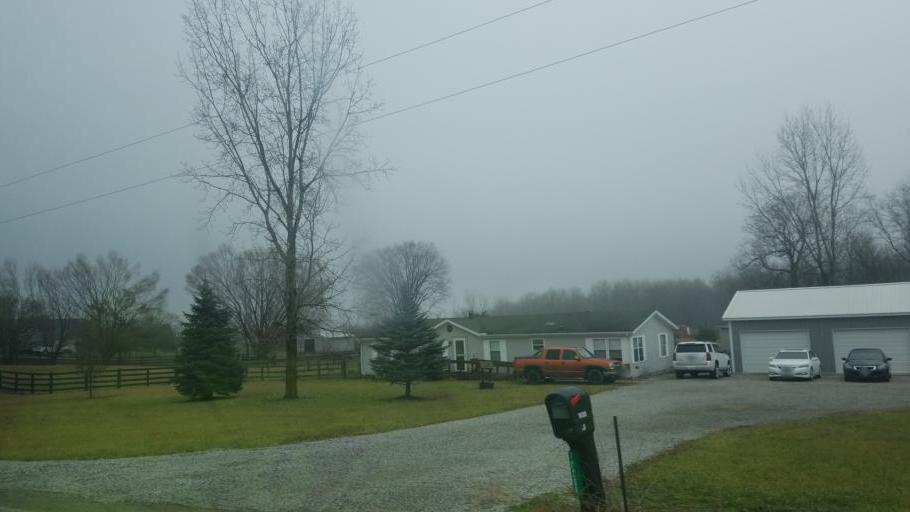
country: US
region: Ohio
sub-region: Champaign County
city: North Lewisburg
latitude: 40.2742
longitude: -83.6027
